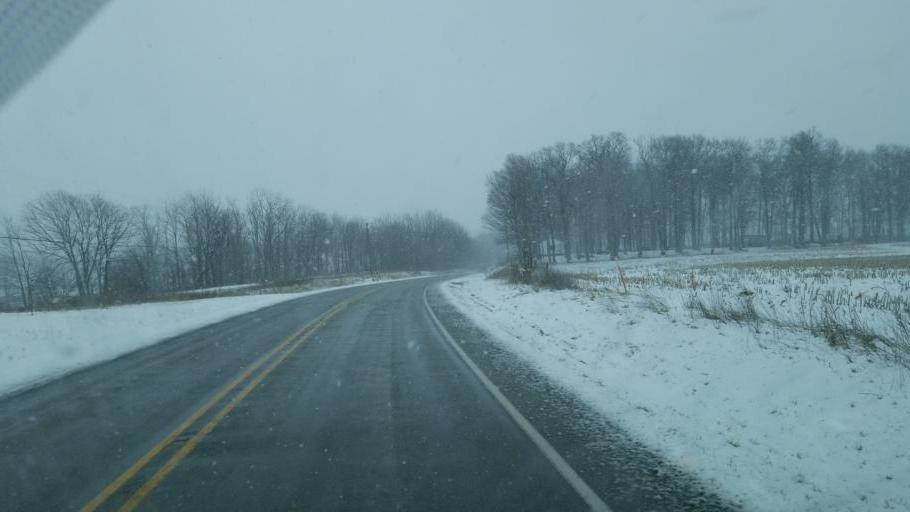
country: US
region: Indiana
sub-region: Wayne County
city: Hagerstown
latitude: 40.0190
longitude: -85.1793
